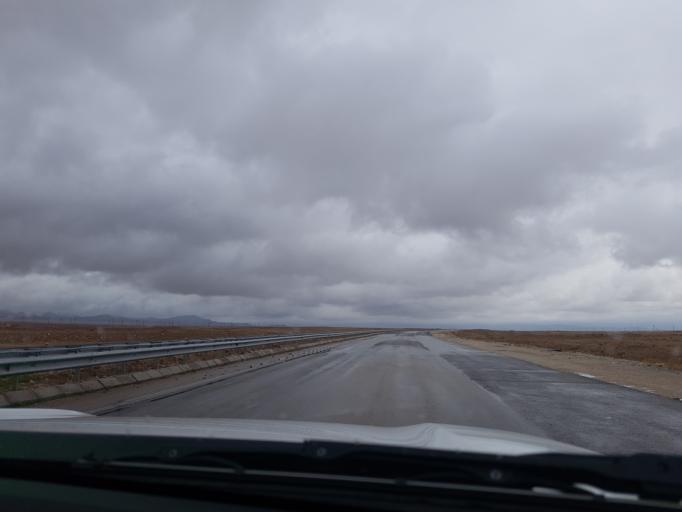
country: TM
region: Balkan
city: Balkanabat
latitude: 39.8959
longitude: 54.0112
